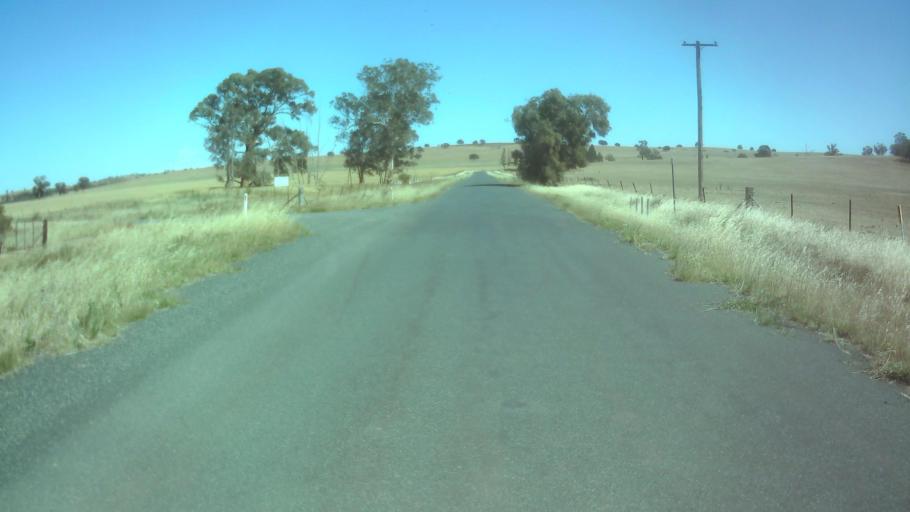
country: AU
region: New South Wales
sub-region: Weddin
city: Grenfell
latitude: -33.9837
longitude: 148.4048
